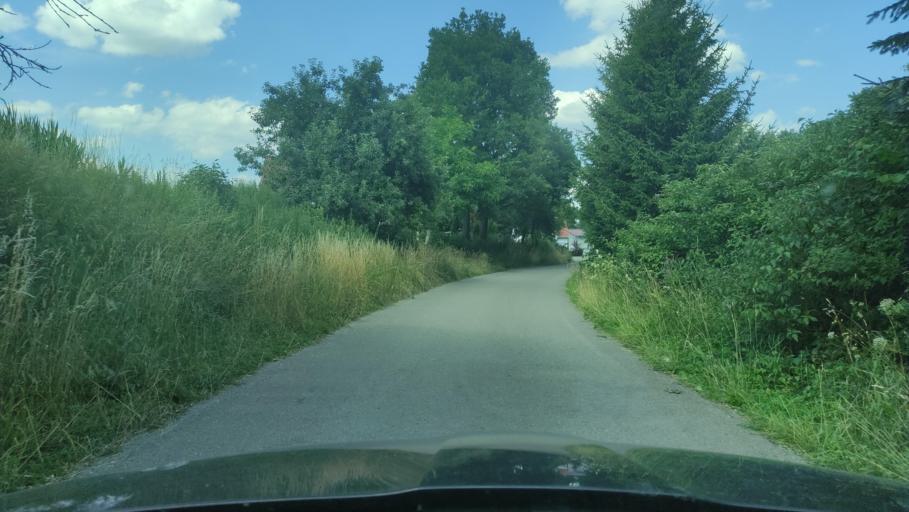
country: DE
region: Bavaria
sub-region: Swabia
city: Deisenhausen
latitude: 48.2876
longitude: 10.3000
